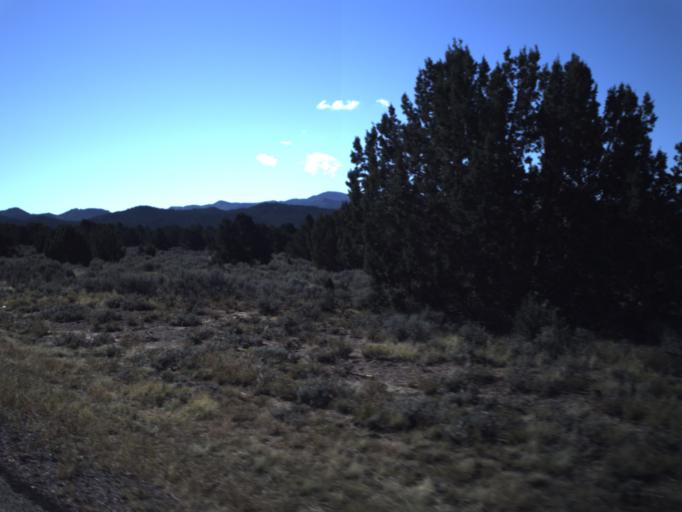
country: US
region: Utah
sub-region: Washington County
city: Enterprise
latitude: 37.6325
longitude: -113.4286
